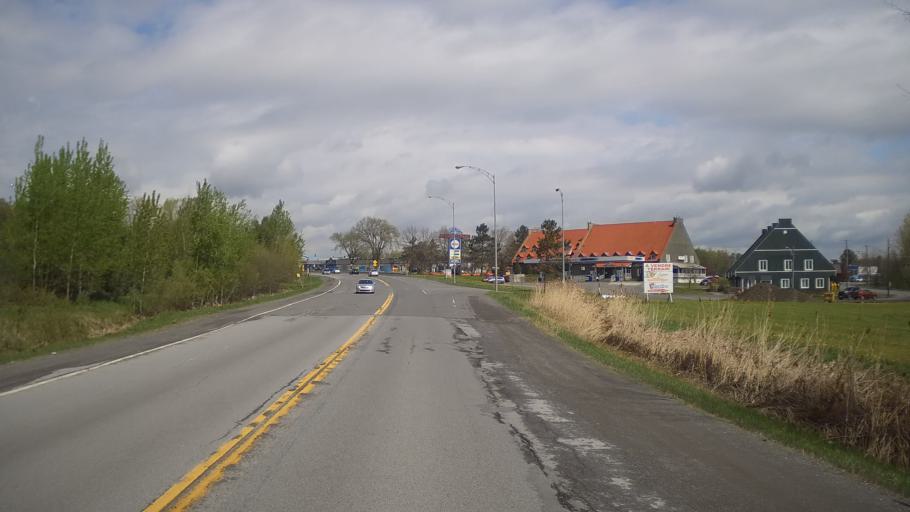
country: CA
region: Quebec
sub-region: Monteregie
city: Cowansville
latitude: 45.2074
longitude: -72.7676
